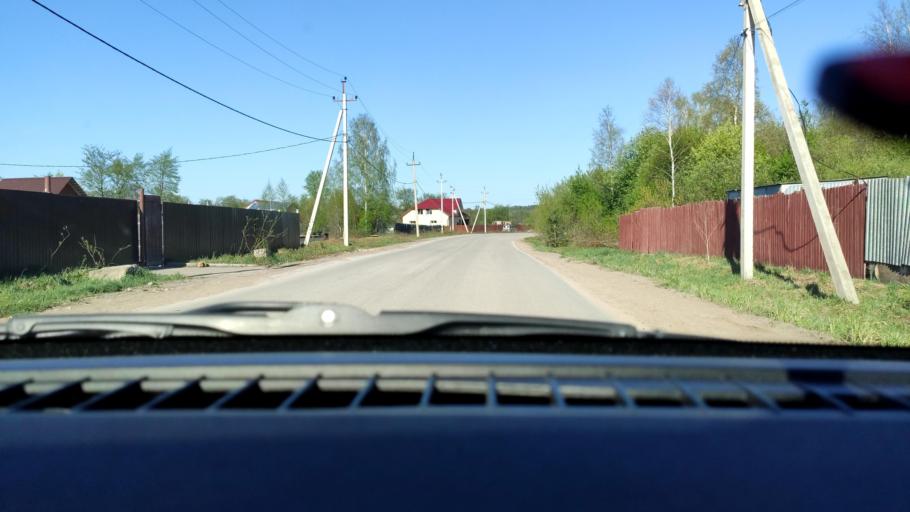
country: RU
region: Perm
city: Overyata
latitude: 58.0778
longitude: 55.9858
